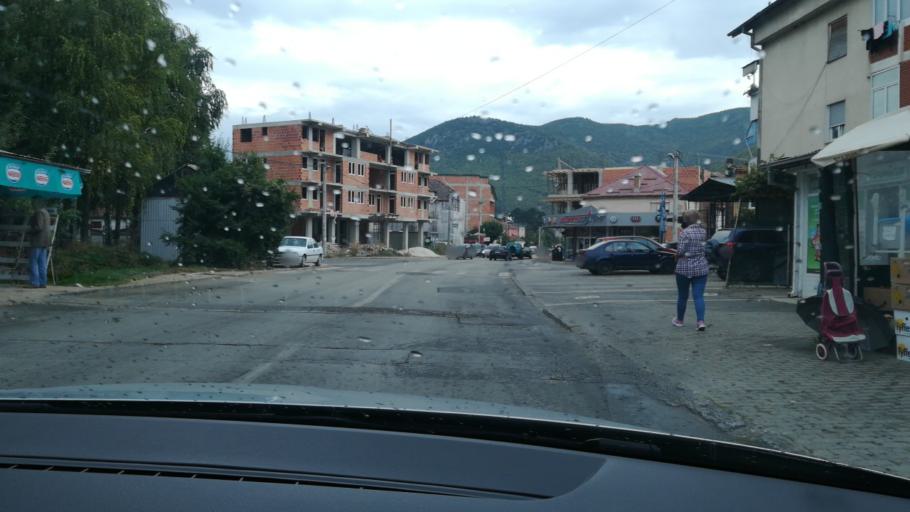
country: MK
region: Kicevo
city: Kicevo
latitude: 41.5083
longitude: 20.9562
